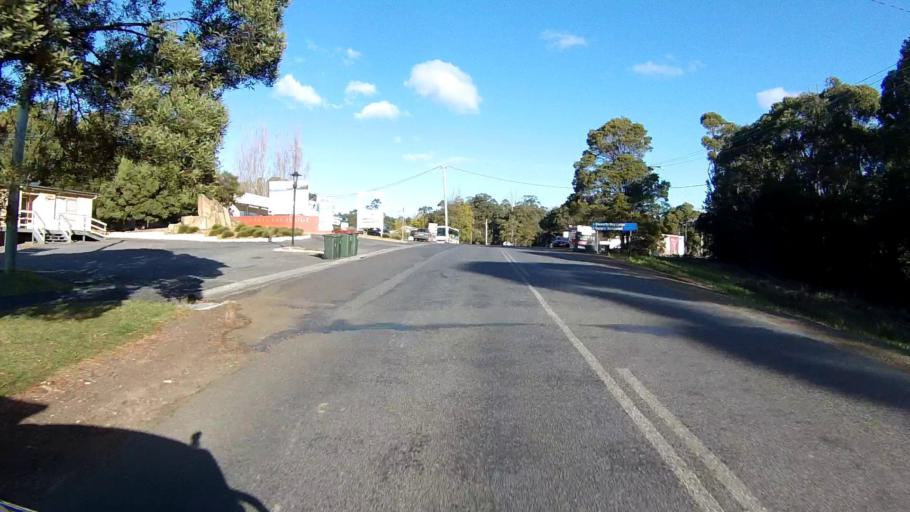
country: AU
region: Tasmania
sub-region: Clarence
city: Sandford
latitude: -43.1391
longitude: 147.8507
